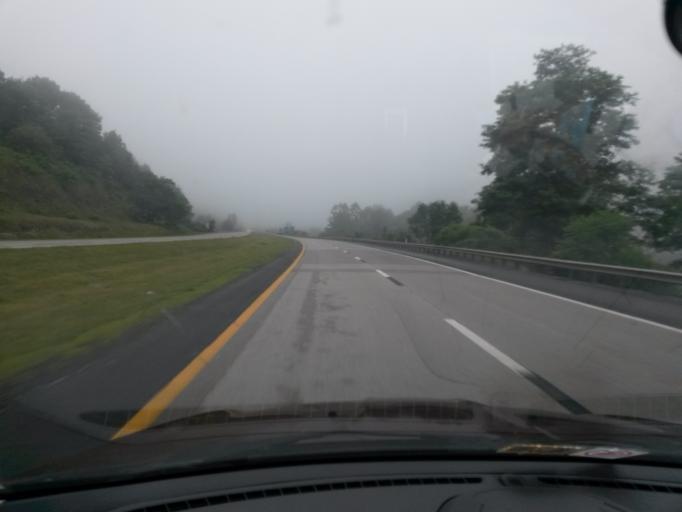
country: US
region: West Virginia
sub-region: Greenbrier County
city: Rainelle
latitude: 37.8194
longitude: -80.8127
